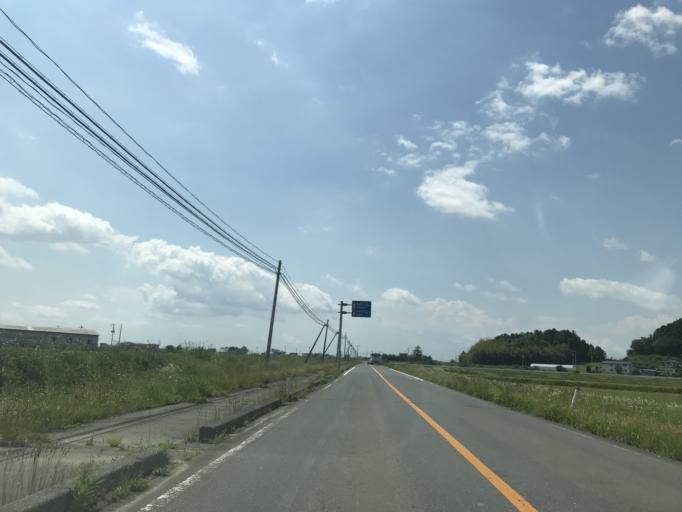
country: JP
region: Miyagi
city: Kogota
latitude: 38.6126
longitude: 141.0208
